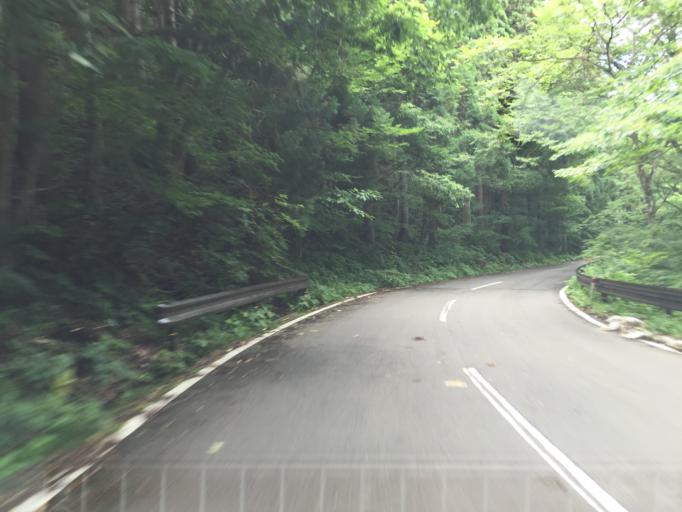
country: JP
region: Fukushima
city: Nihommatsu
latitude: 37.6718
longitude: 140.3311
